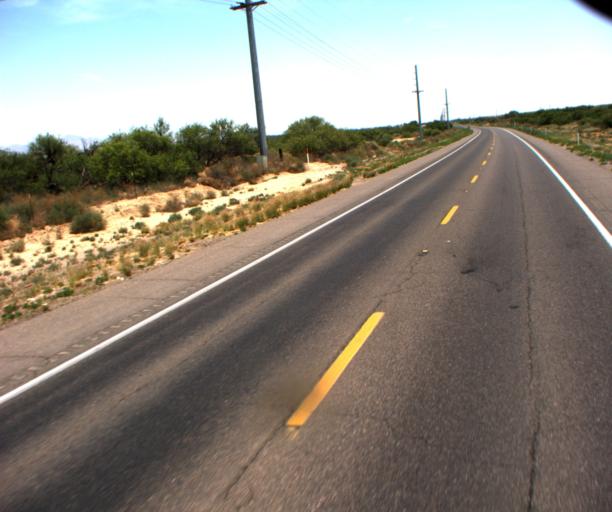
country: US
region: Arizona
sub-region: Graham County
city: Pima
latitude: 32.9395
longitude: -109.9052
